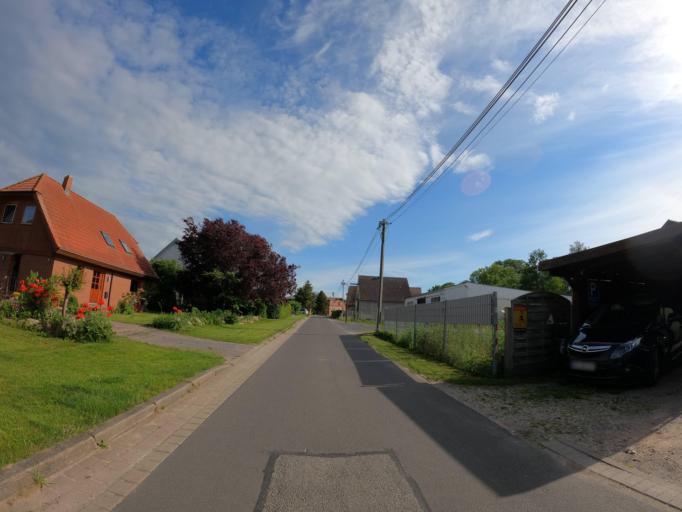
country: DE
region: Mecklenburg-Vorpommern
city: Preetz
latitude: 54.3482
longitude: 13.0101
